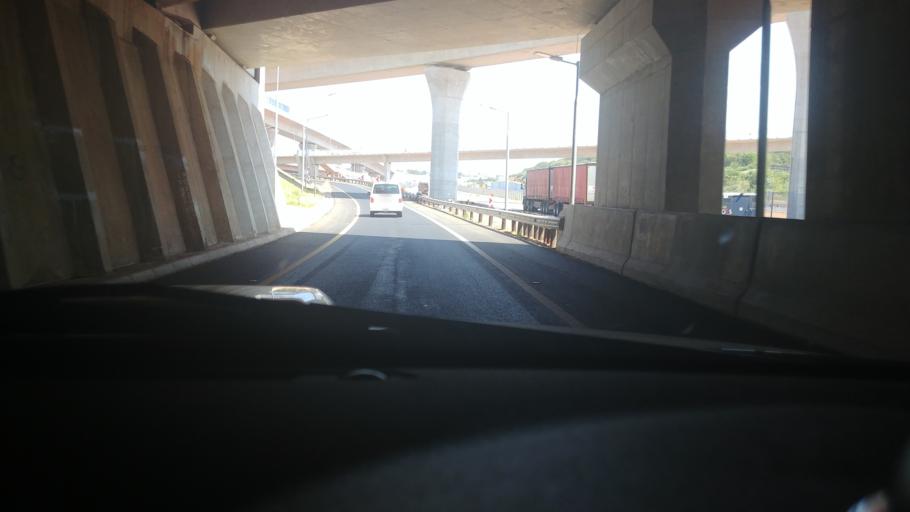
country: ZA
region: KwaZulu-Natal
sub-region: eThekwini Metropolitan Municipality
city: Durban
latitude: -29.7234
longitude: 31.0589
